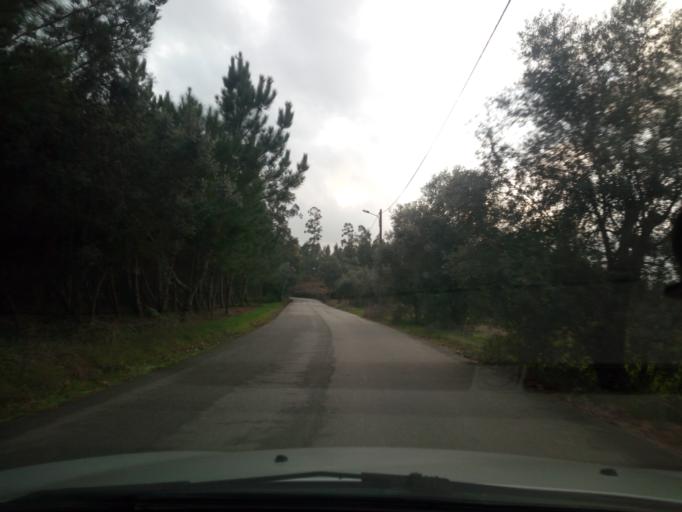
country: PT
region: Aveiro
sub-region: Oliveira do Bairro
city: Oliveira do Bairro
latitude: 40.5517
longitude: -8.4790
